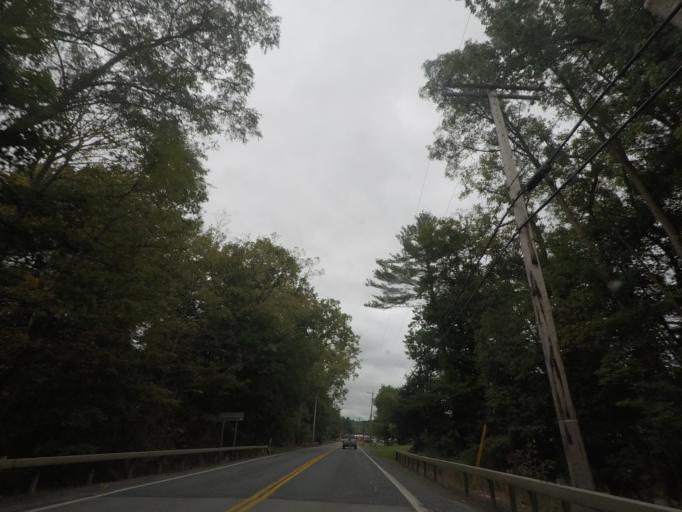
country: US
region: New York
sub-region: Rensselaer County
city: Hoosick Falls
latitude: 42.9510
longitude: -73.3817
